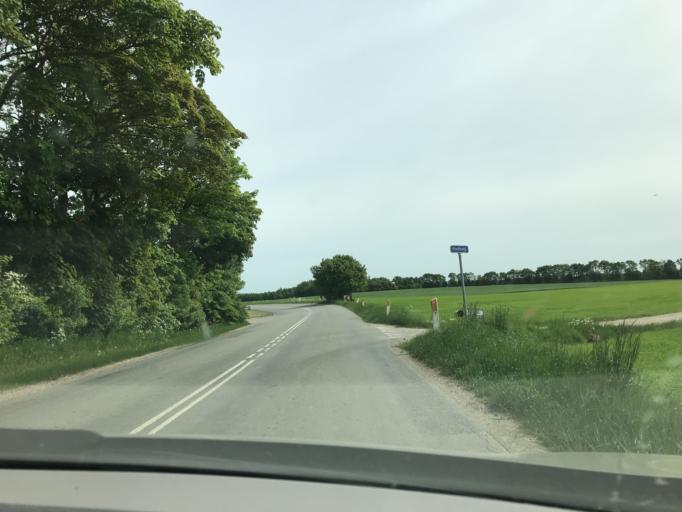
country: DK
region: Central Jutland
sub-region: Norddjurs Kommune
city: Allingabro
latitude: 56.5384
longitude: 10.3000
